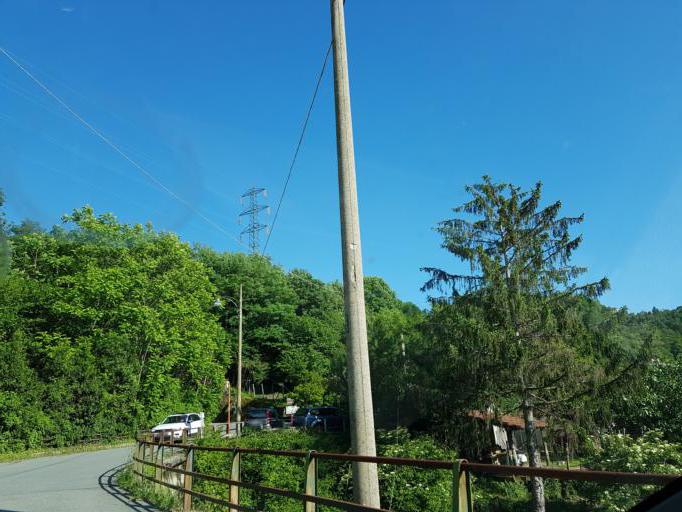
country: IT
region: Liguria
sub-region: Provincia di Genova
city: Manesseno
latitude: 44.4720
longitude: 8.9169
